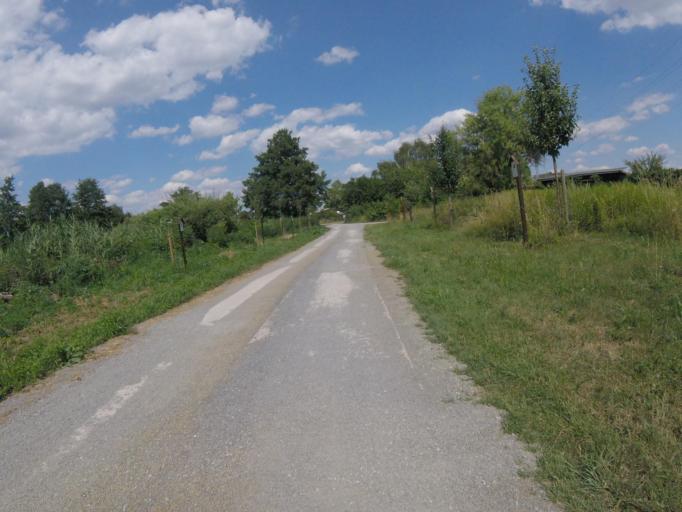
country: DE
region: Brandenburg
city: Wildau
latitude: 52.3287
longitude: 13.6443
